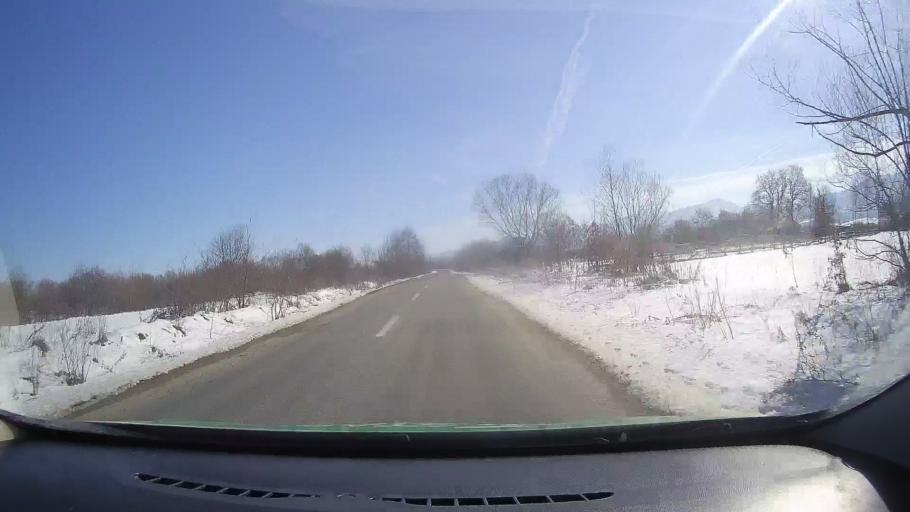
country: RO
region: Brasov
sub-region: Comuna Harseni
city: Harseni
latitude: 45.7319
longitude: 25.0200
